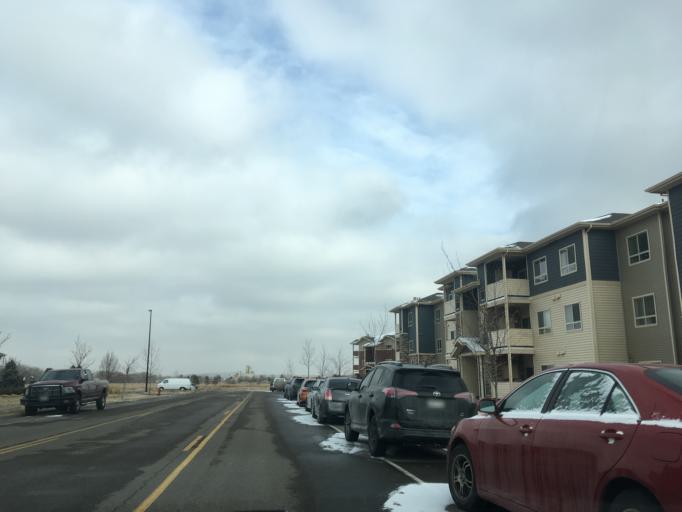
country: US
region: Colorado
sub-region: Boulder County
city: Lafayette
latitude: 39.9747
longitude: -105.0821
